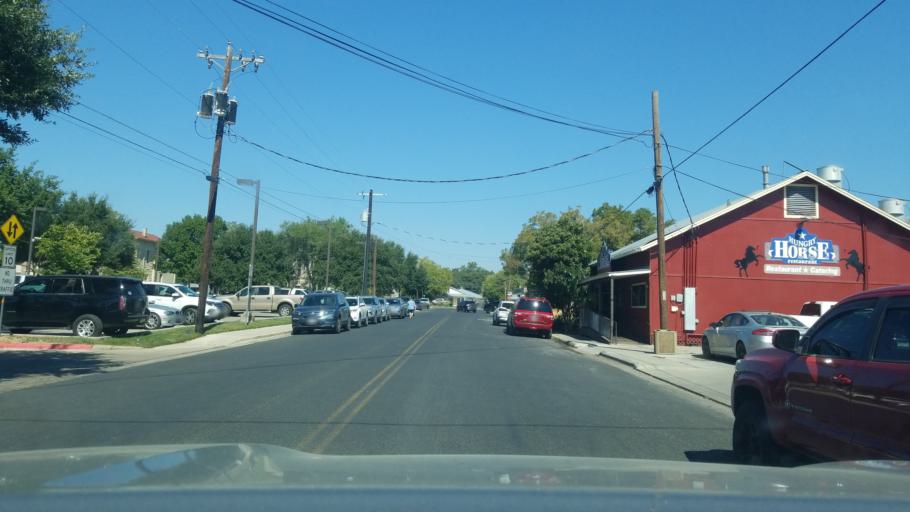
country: US
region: Texas
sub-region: Kendall County
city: Boerne
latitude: 29.7938
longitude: -98.7298
